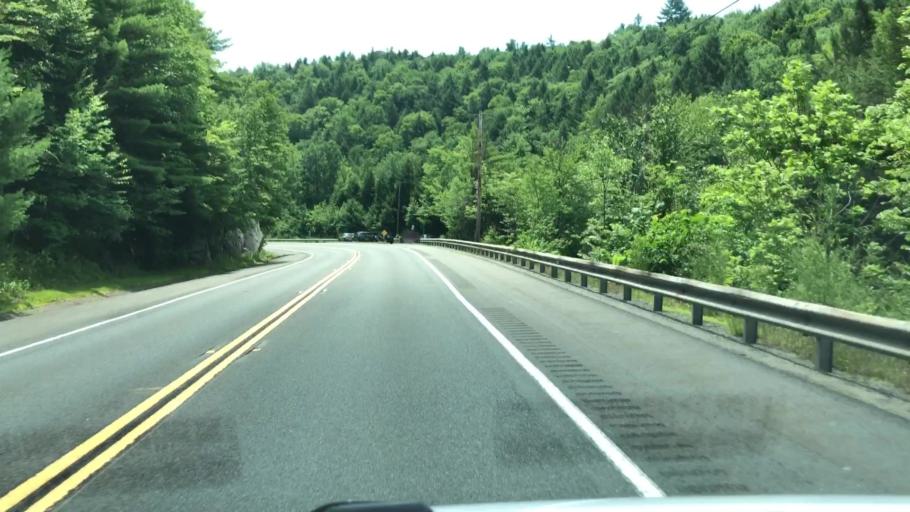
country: US
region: Massachusetts
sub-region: Hampshire County
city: Chesterfield
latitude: 42.4422
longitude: -72.8691
